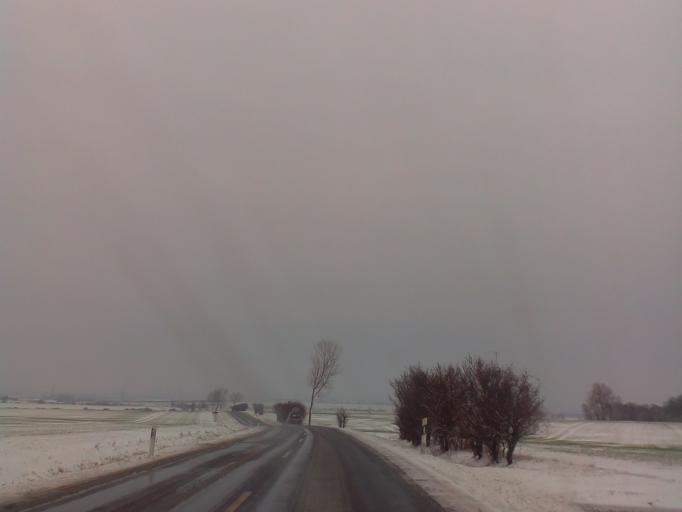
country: DE
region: Thuringia
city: Behringen
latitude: 50.8037
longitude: 11.0332
